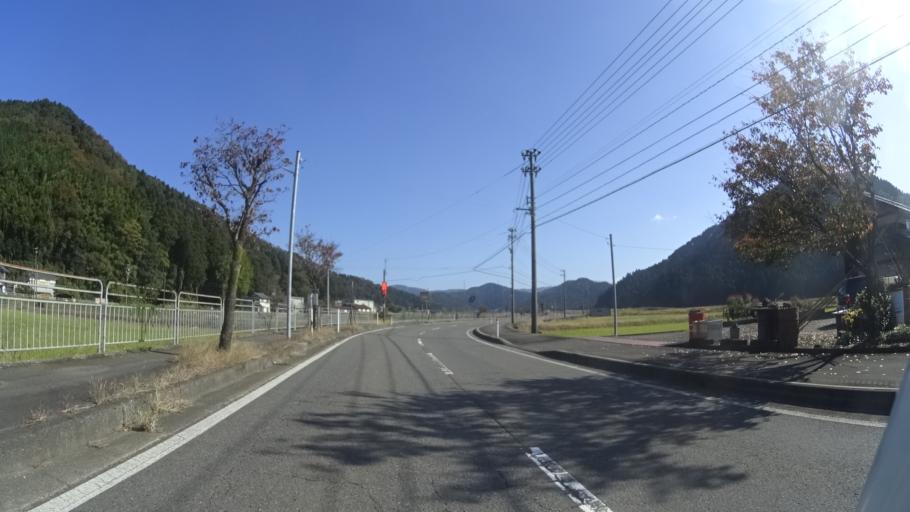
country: JP
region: Fukui
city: Sabae
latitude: 35.9488
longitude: 136.2492
